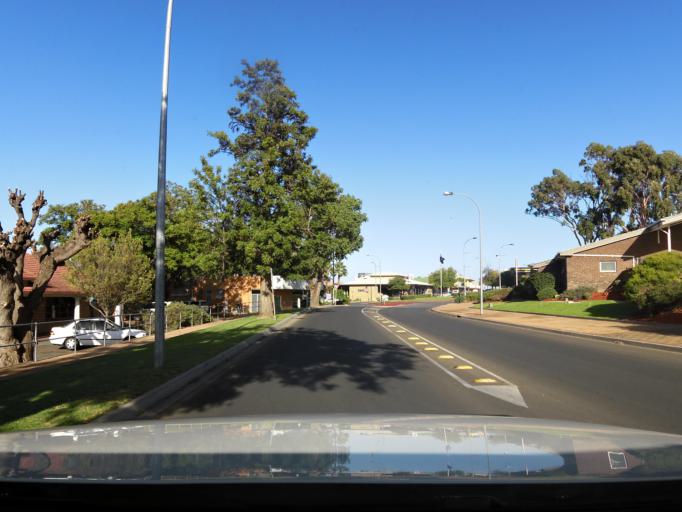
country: AU
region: South Australia
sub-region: Berri and Barmera
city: Berri
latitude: -34.2850
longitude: 140.6026
